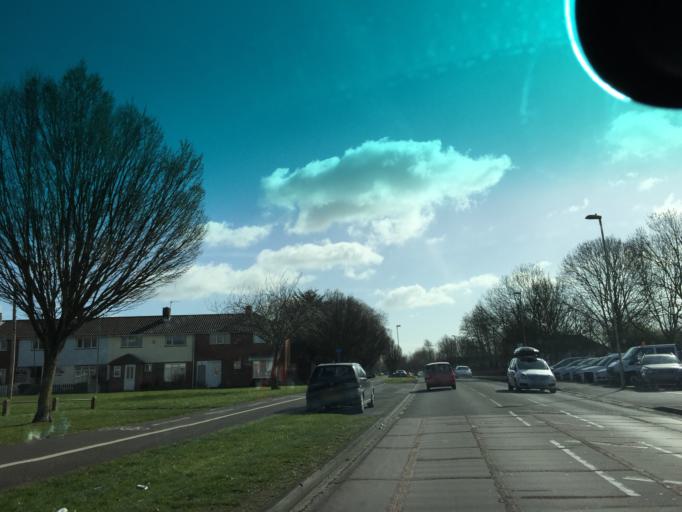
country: GB
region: England
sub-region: Hampshire
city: Lee-on-the-Solent
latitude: 50.8119
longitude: -1.1684
